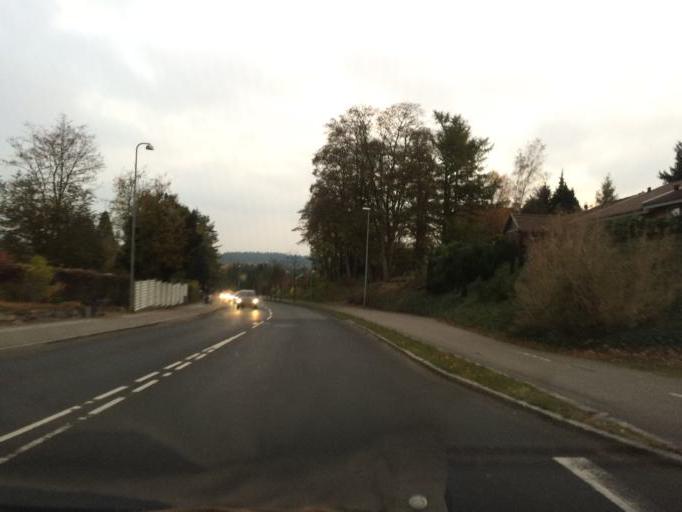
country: DK
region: Central Jutland
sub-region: Silkeborg Kommune
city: Silkeborg
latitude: 56.1787
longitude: 9.5193
